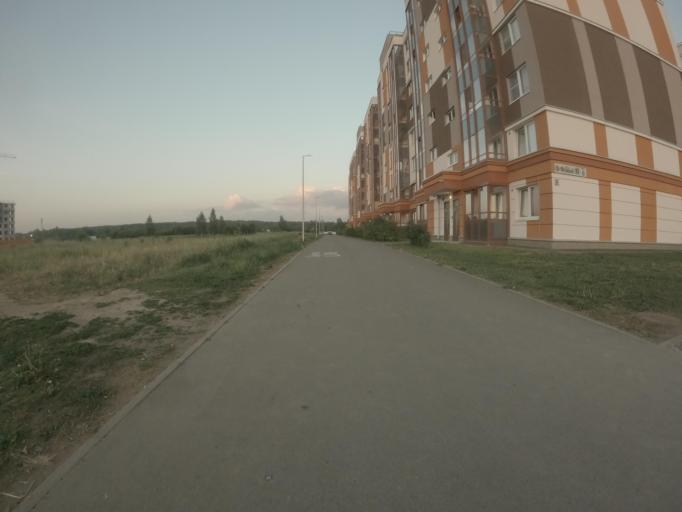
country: RU
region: Leningrad
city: Yanino Vtoroye
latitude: 59.9598
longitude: 30.6021
